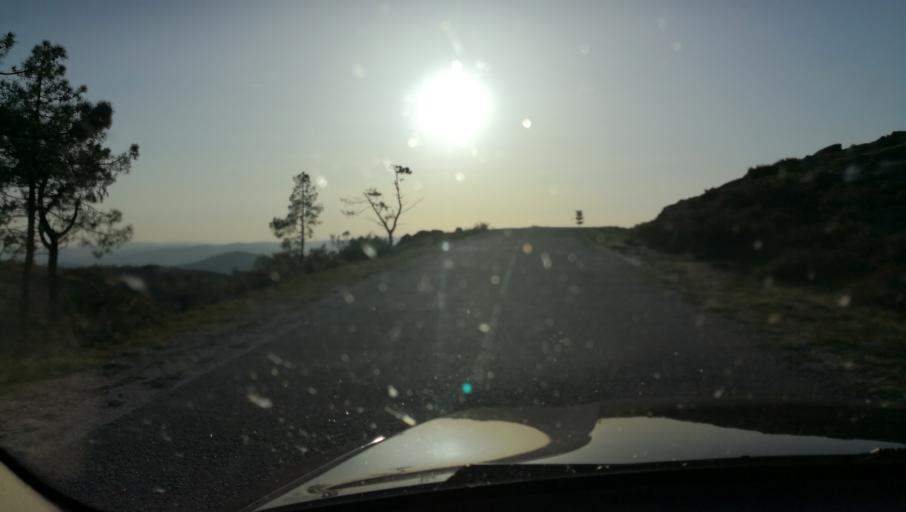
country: PT
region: Vila Real
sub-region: Vila Real
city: Vila Real
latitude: 41.3809
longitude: -7.8194
